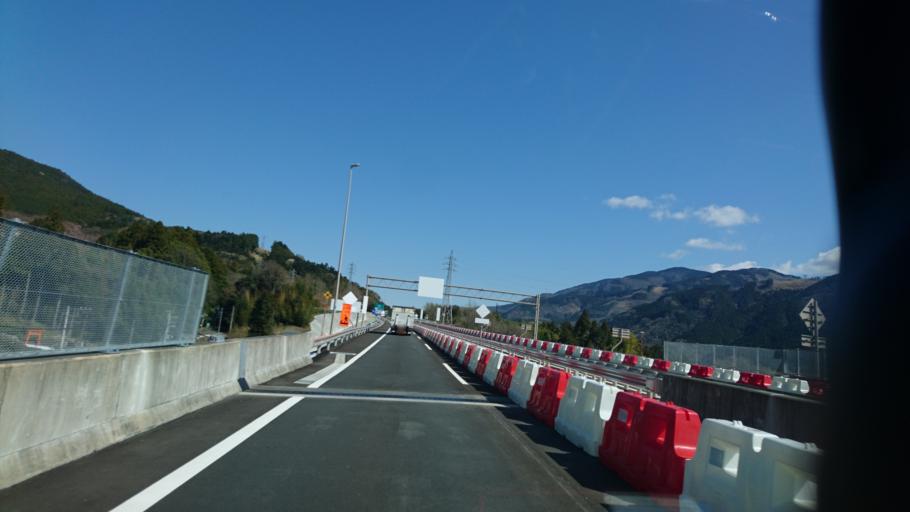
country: JP
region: Shizuoka
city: Fujinomiya
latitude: 35.2952
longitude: 138.4436
